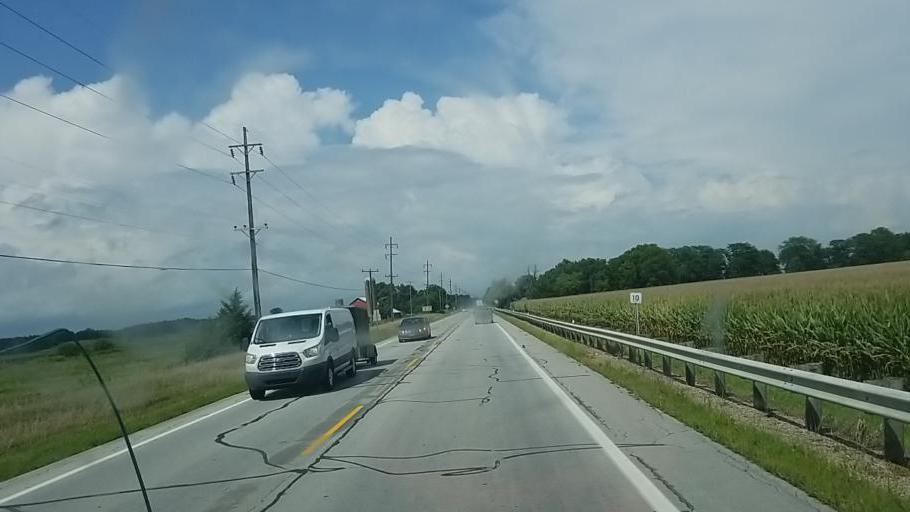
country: US
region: Ohio
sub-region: Champaign County
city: Urbana
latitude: 40.1563
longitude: -83.7457
